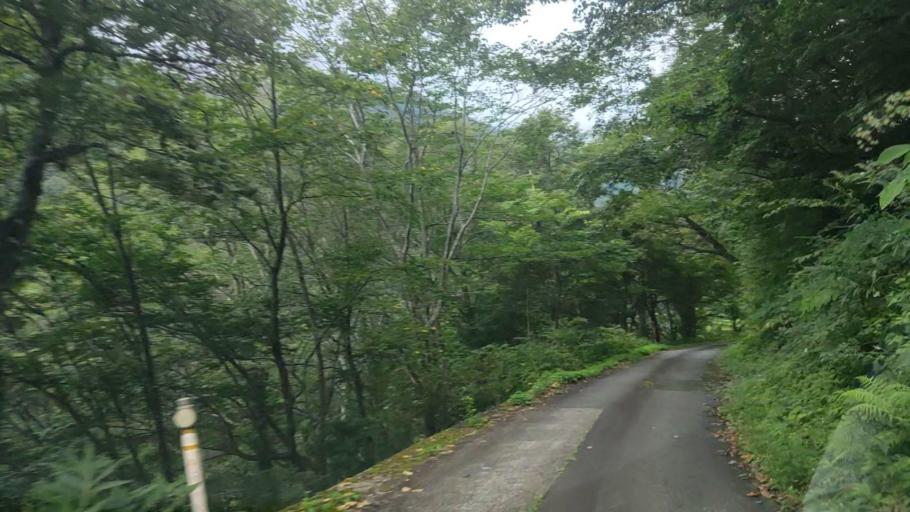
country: JP
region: Toyama
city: Yatsuomachi-higashikumisaka
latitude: 36.3980
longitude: 137.0743
